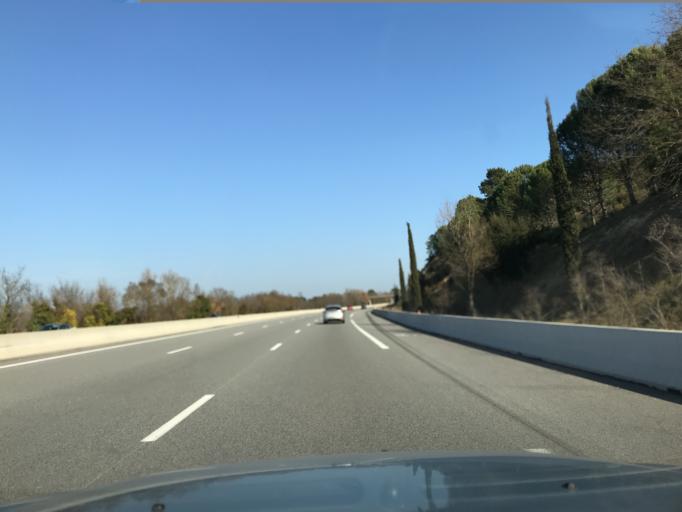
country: FR
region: Provence-Alpes-Cote d'Azur
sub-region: Departement du Var
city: Les Arcs
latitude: 43.4500
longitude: 6.5009
